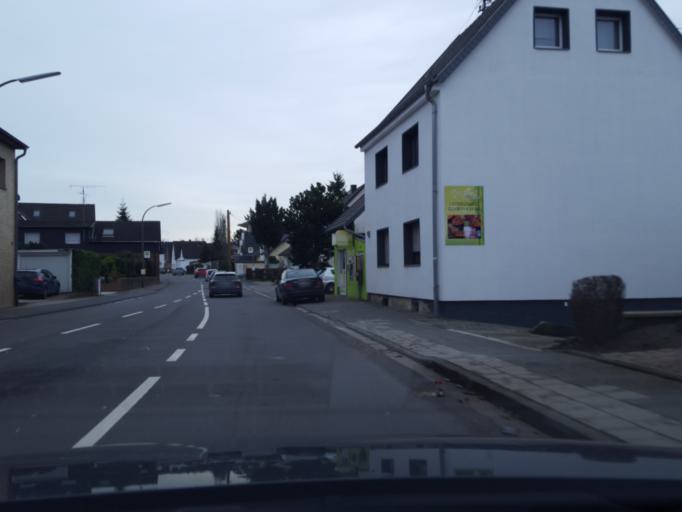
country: DE
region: North Rhine-Westphalia
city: Niederkassel
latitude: 50.7951
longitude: 7.0496
